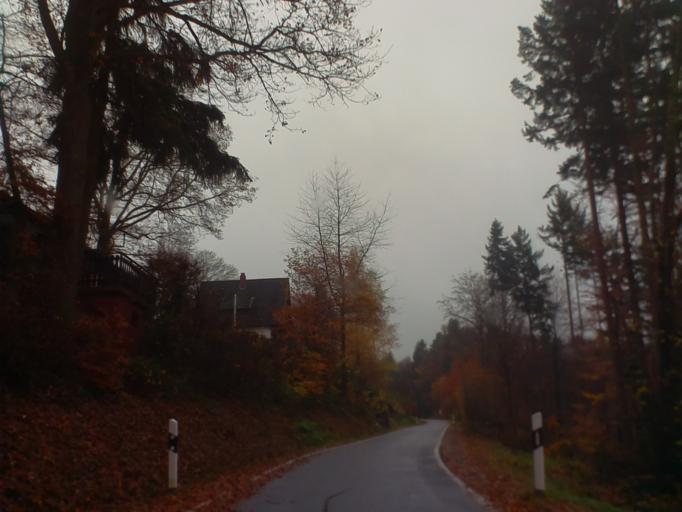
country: DE
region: Hesse
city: Neckarsteinach
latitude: 49.4371
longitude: 8.8470
